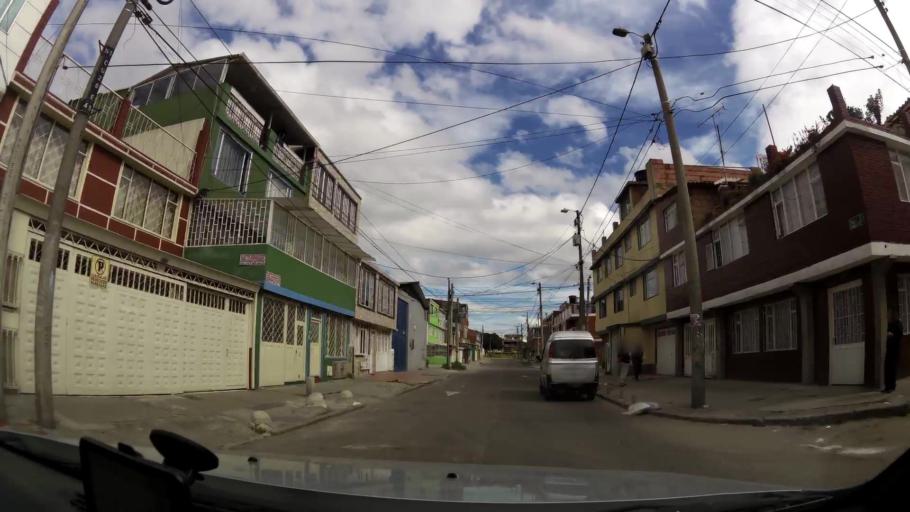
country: CO
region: Bogota D.C.
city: Bogota
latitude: 4.6164
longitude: -74.1070
